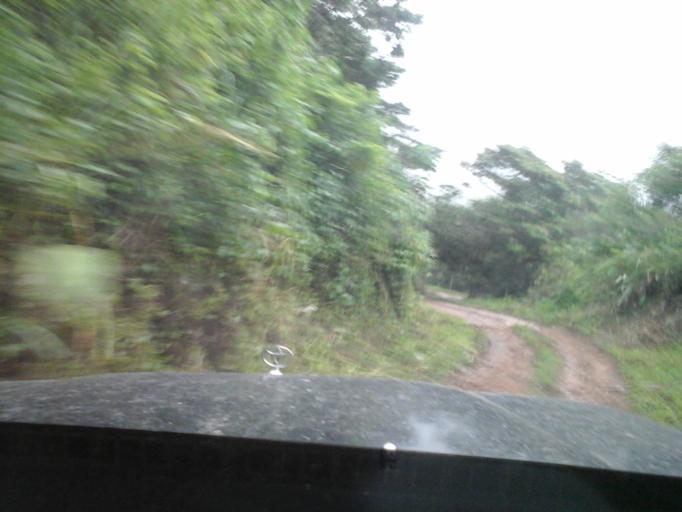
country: CO
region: Cesar
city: Agustin Codazzi
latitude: 9.9399
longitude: -73.1331
